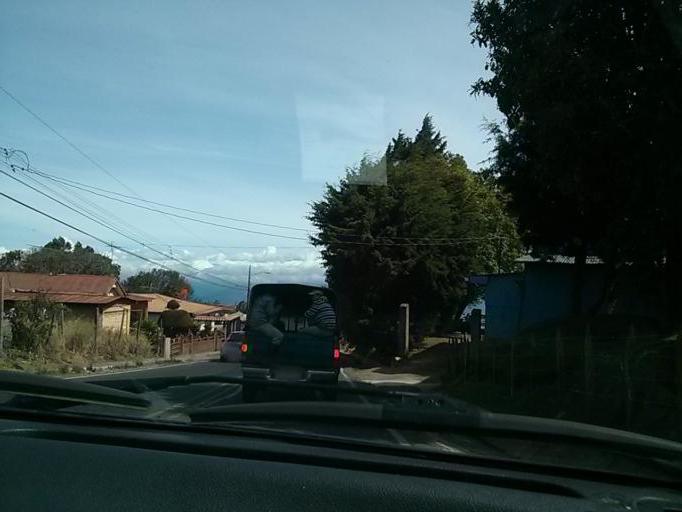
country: CR
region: Cartago
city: Cot
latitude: 9.9228
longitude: -83.8796
